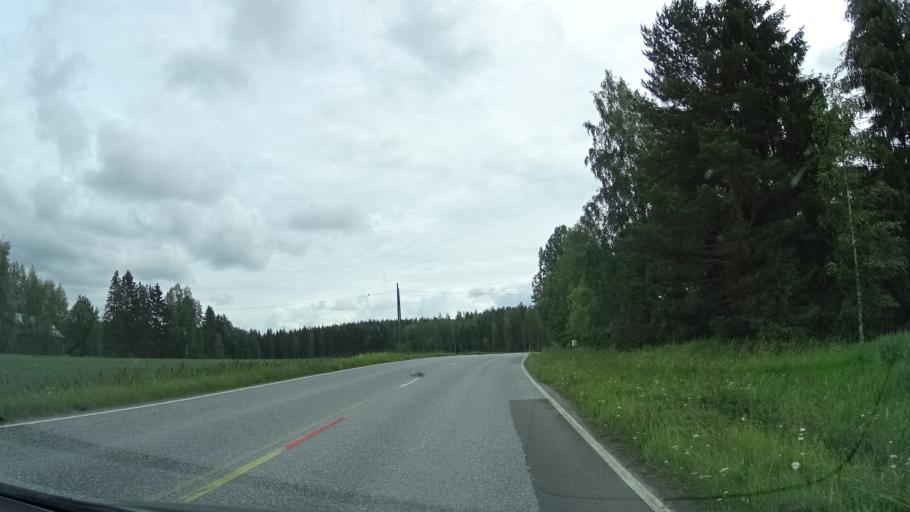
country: FI
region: Pirkanmaa
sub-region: Etelae-Pirkanmaa
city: Urjala
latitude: 61.0904
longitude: 23.5107
